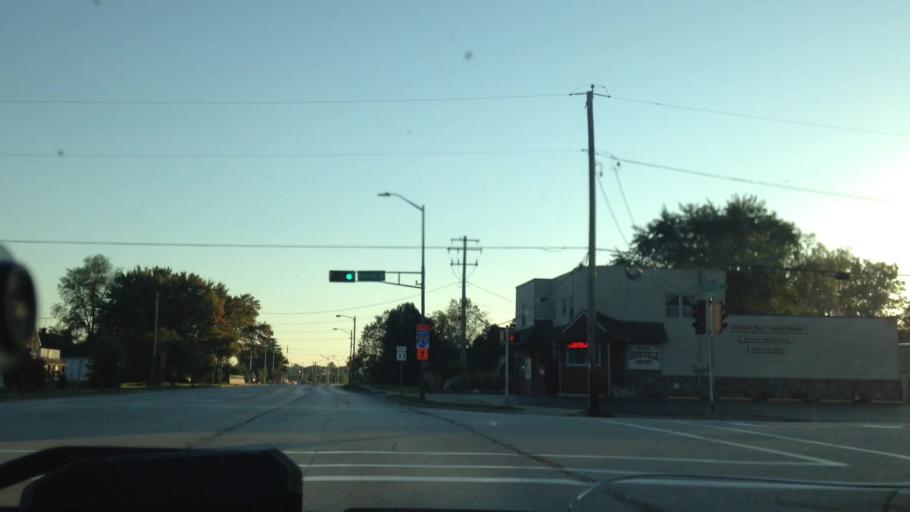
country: US
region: Wisconsin
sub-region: Ozaukee County
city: Saukville
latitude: 43.3827
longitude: -87.9351
